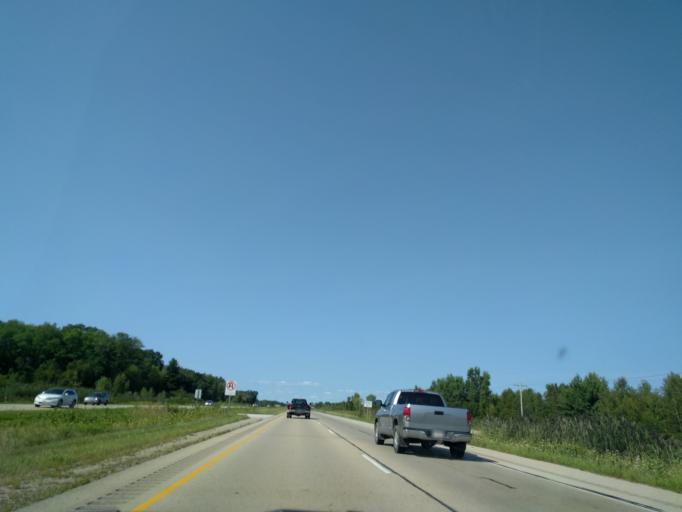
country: US
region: Wisconsin
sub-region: Brown County
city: Suamico
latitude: 44.6867
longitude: -88.0503
